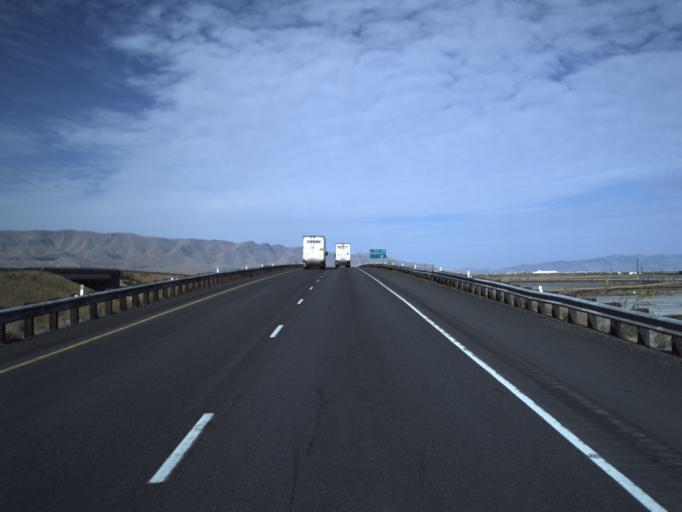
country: US
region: Utah
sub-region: Tooele County
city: Grantsville
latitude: 40.6839
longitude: -112.4375
